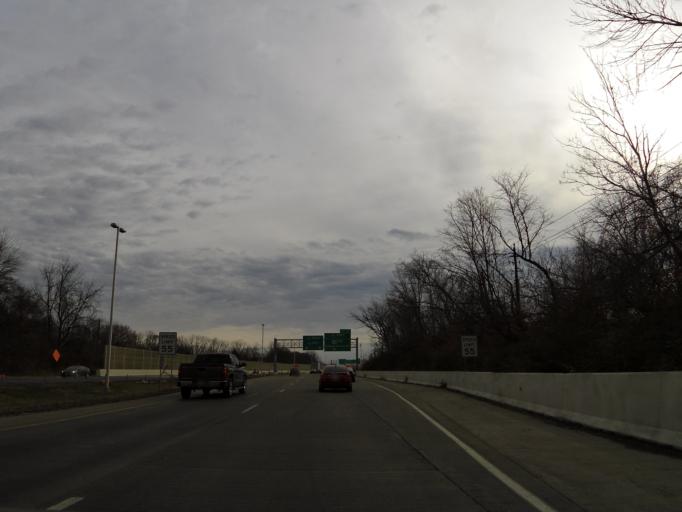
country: US
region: Indiana
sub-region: Marion County
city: Speedway
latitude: 39.8112
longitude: -86.2862
